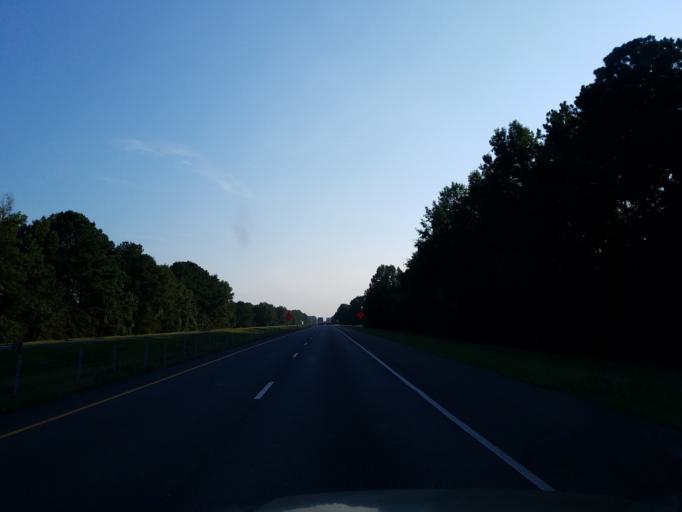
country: US
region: Alabama
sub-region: Sumter County
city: Livingston
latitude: 32.7511
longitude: -88.0823
